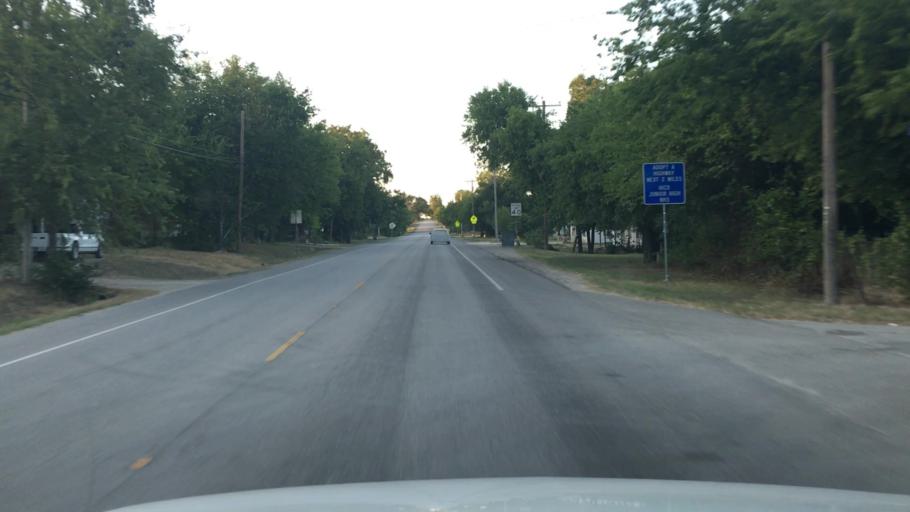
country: US
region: Texas
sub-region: Hamilton County
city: Hico
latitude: 31.9843
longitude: -98.0279
